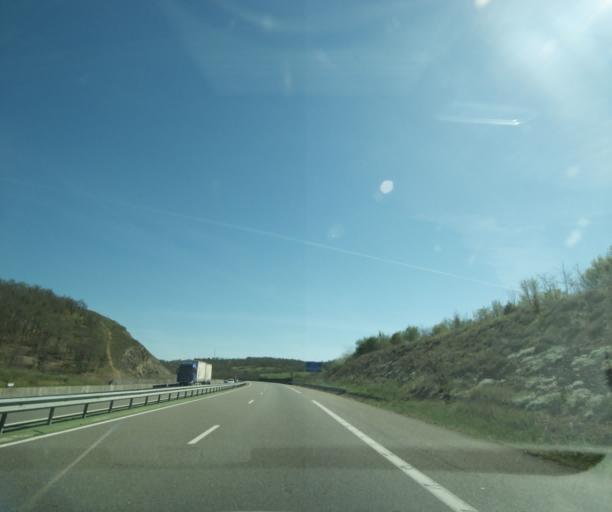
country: FR
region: Midi-Pyrenees
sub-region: Departement du Lot
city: Cahors
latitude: 44.4205
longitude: 1.5108
